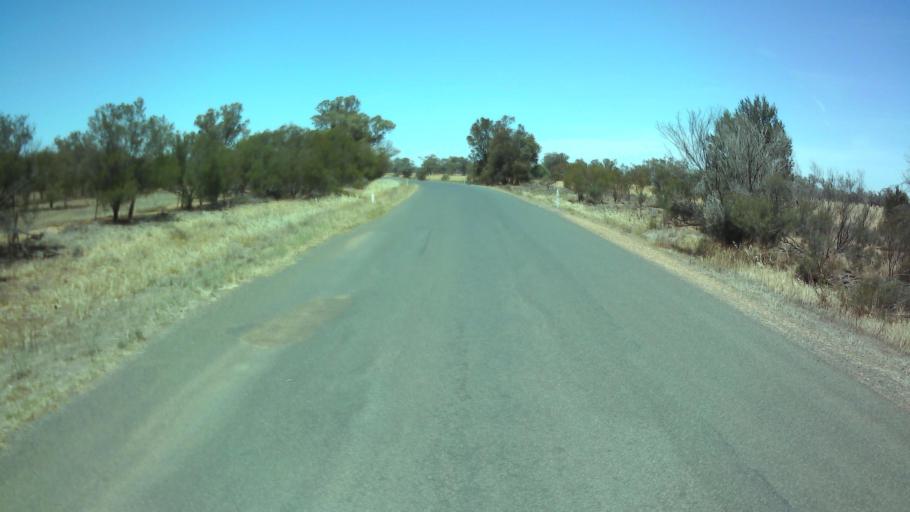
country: AU
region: New South Wales
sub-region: Weddin
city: Grenfell
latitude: -34.0582
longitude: 147.7798
